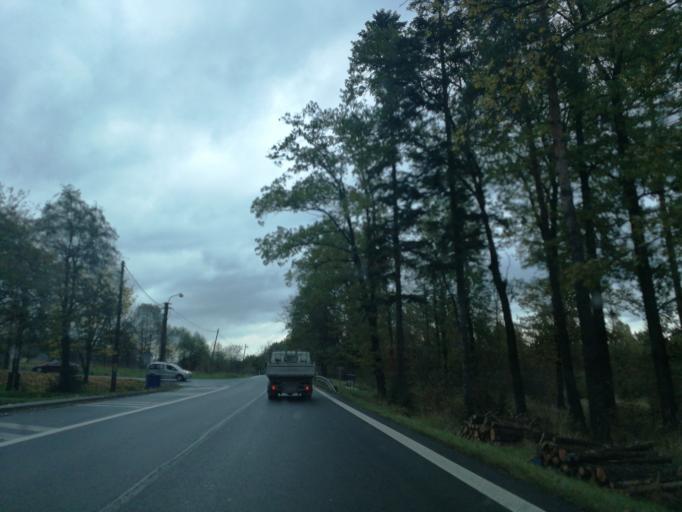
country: CZ
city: Hodslavice
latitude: 49.5236
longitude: 18.0157
